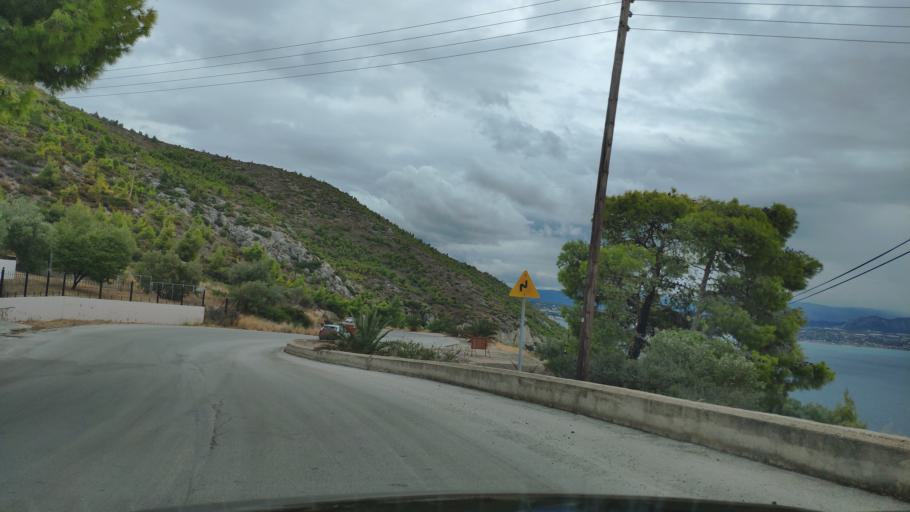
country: GR
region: Peloponnese
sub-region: Nomos Korinthias
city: Perachora
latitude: 37.9993
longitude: 22.9463
